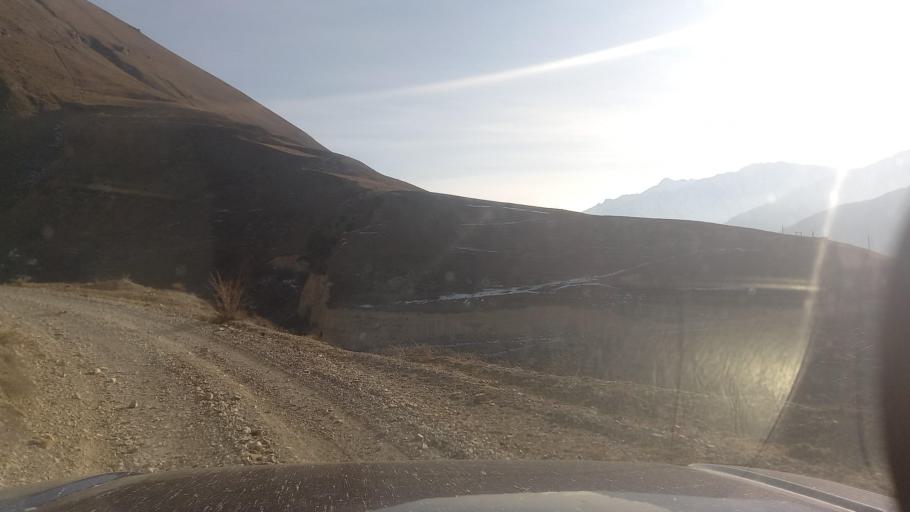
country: RU
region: Ingushetiya
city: Dzhayrakh
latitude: 42.8451
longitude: 44.6603
